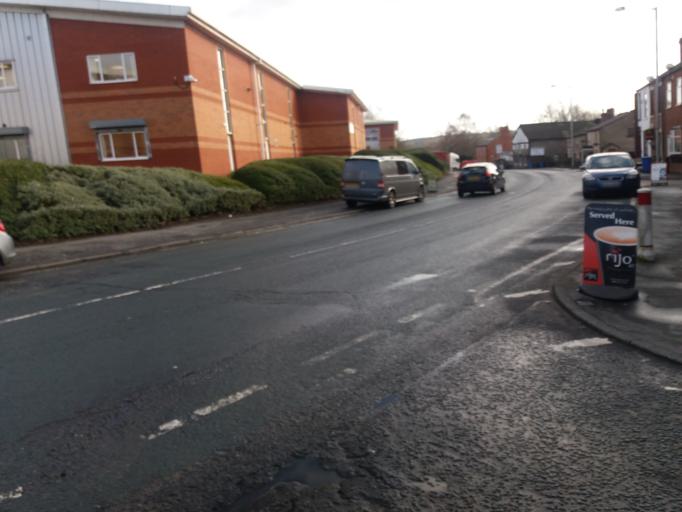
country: GB
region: England
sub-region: Lancashire
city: Adlington
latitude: 53.6104
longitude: -2.6053
